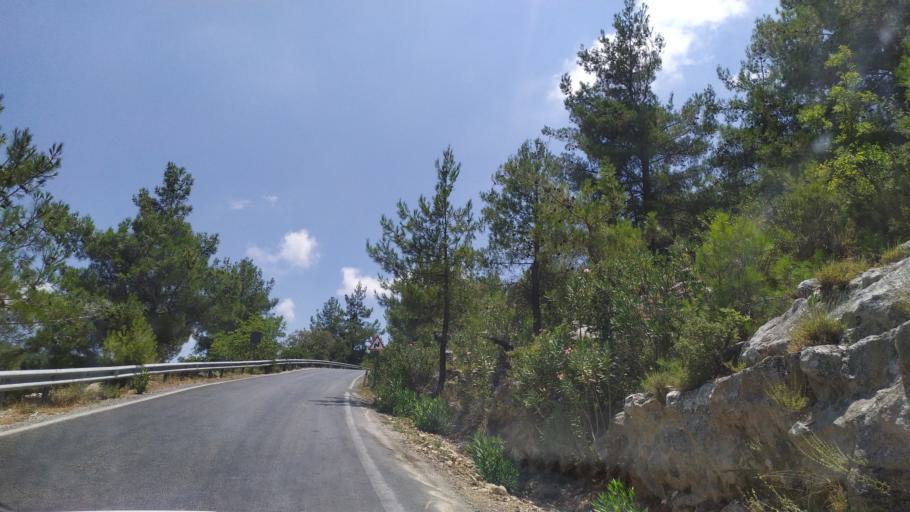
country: TR
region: Mersin
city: Gulnar
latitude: 36.2772
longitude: 33.3799
